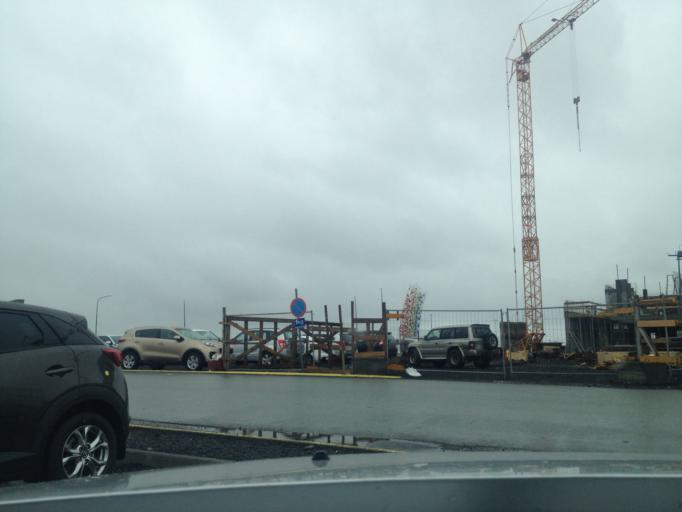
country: IS
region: Southern Peninsula
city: Reykjanesbaer
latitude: 63.9982
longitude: -22.6299
